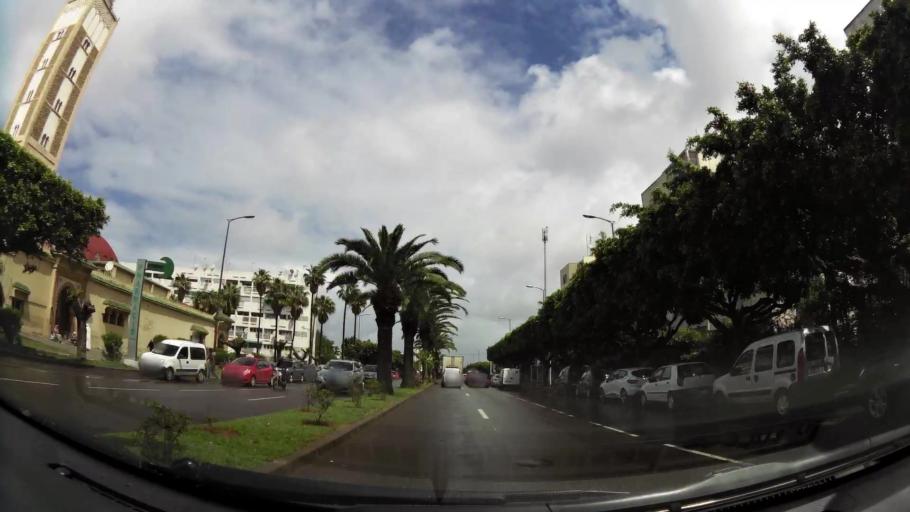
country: MA
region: Grand Casablanca
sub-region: Casablanca
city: Casablanca
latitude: 33.5700
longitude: -7.6360
